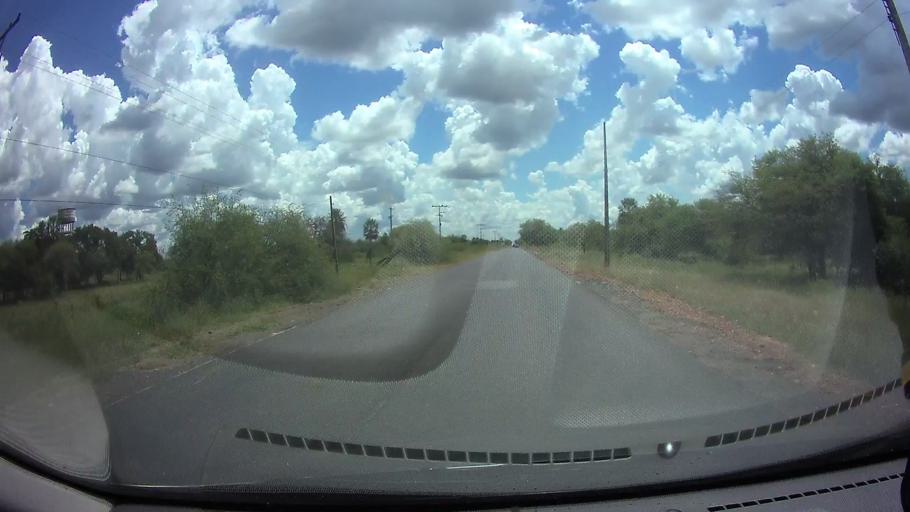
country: PY
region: Presidente Hayes
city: Nanawa
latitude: -25.2359
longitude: -57.6875
